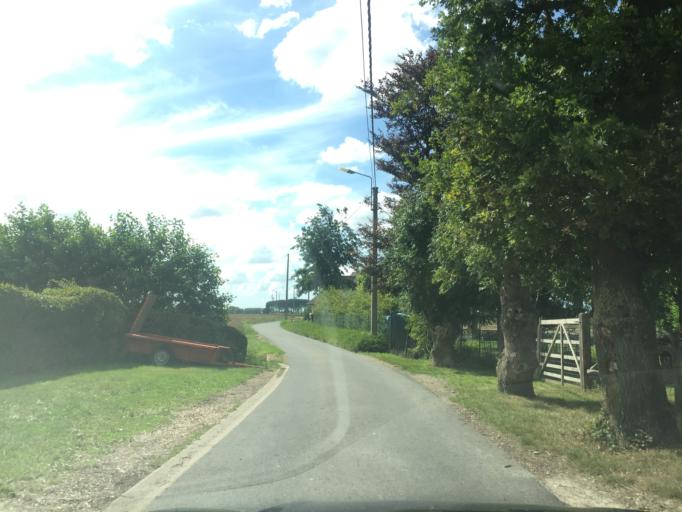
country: BE
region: Flanders
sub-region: Provincie West-Vlaanderen
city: Staden
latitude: 50.9843
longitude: 3.0449
